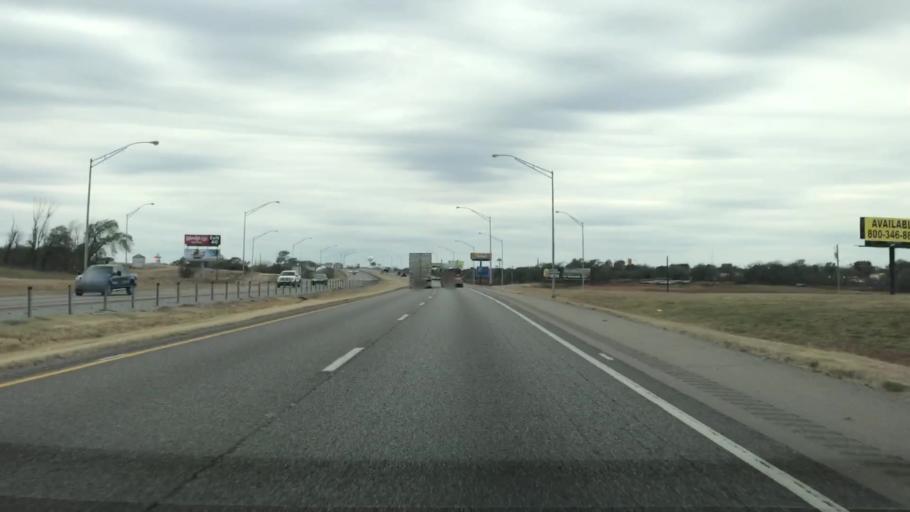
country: US
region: Oklahoma
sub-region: Custer County
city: Clinton
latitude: 35.5007
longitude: -98.9665
